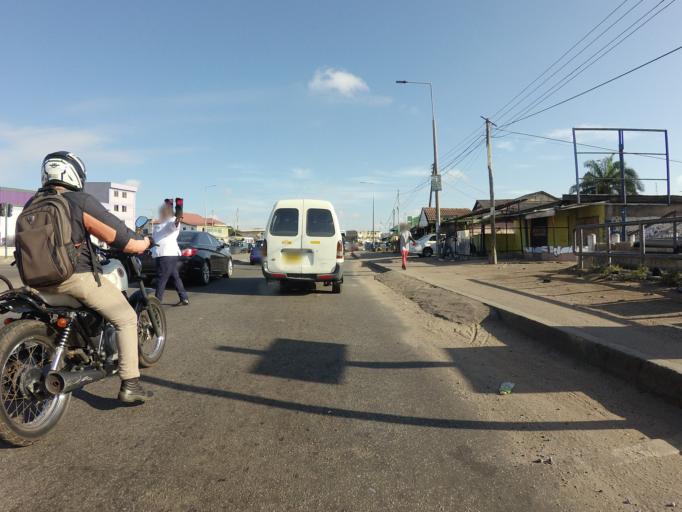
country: GH
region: Greater Accra
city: Accra
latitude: 5.5555
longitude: -0.2318
